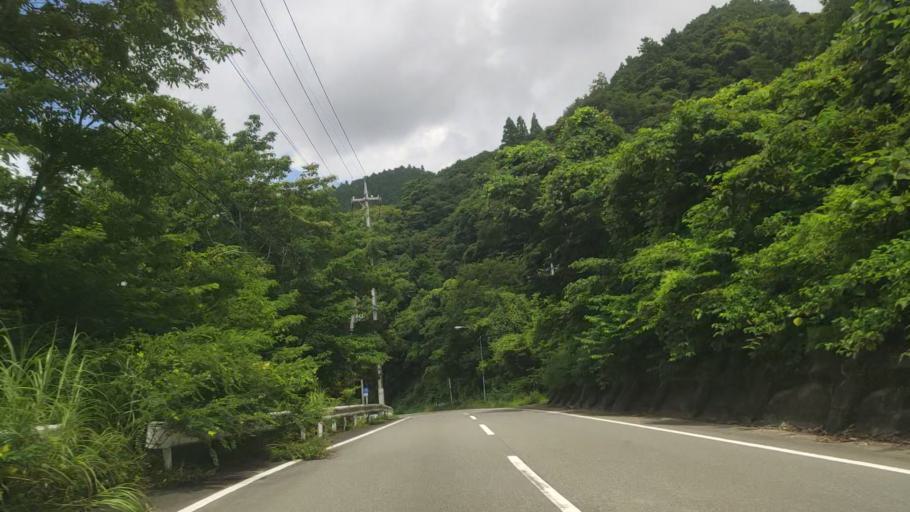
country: JP
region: Shizuoka
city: Fujinomiya
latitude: 35.2505
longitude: 138.4866
